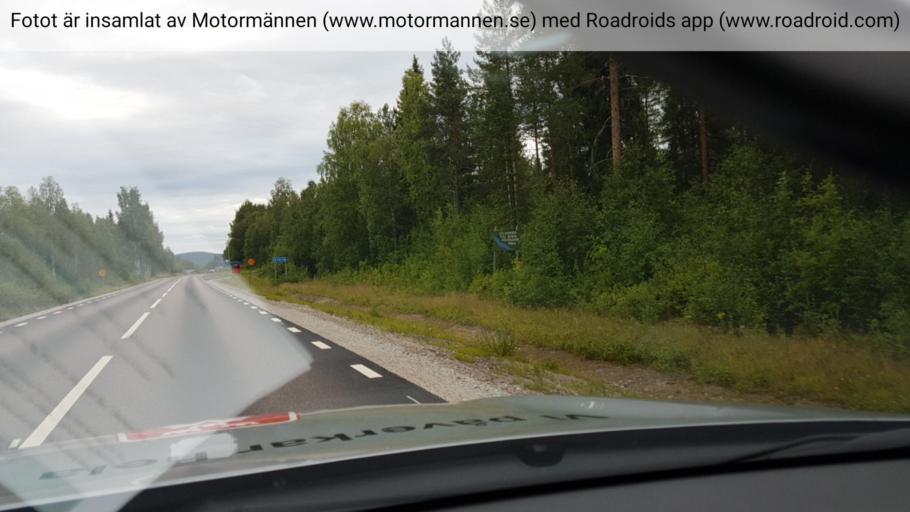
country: SE
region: Norrbotten
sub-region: Overkalix Kommun
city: OEverkalix
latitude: 66.3721
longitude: 22.8427
